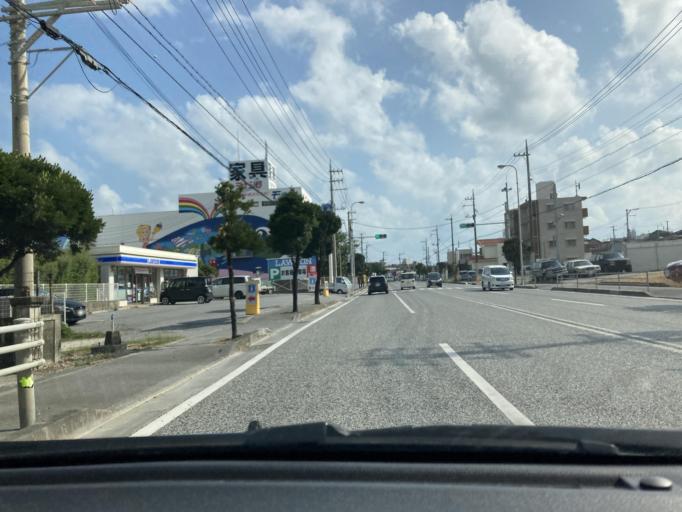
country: JP
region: Okinawa
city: Chatan
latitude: 26.2859
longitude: 127.8151
